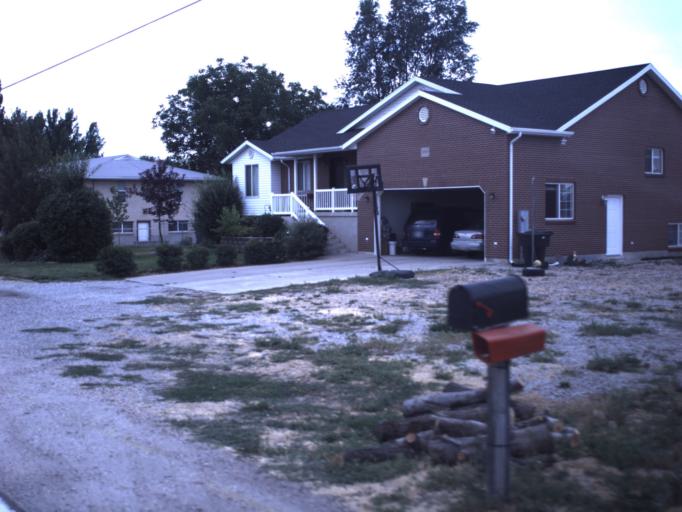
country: US
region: Utah
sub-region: Davis County
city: West Point
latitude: 41.1062
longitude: -112.1127
